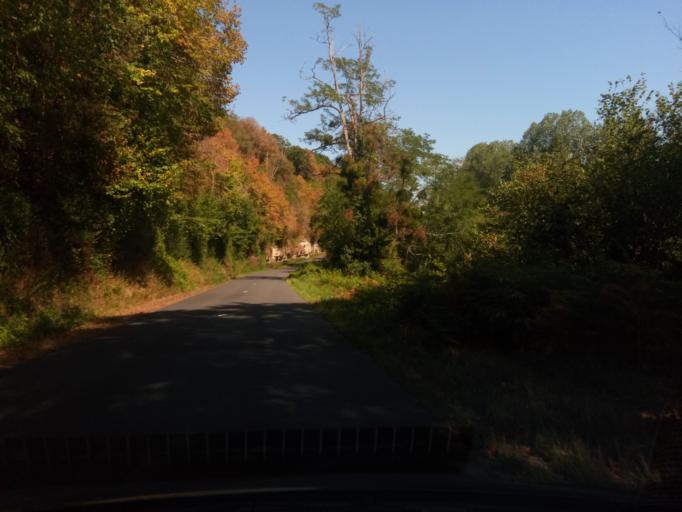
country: FR
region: Poitou-Charentes
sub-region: Departement de la Vienne
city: Saulge
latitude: 46.3827
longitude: 0.8722
